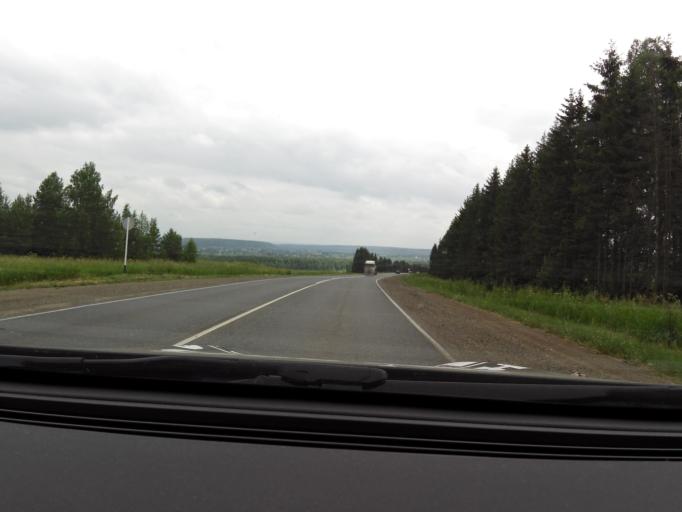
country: RU
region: Perm
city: Kungur
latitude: 57.4754
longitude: 56.7373
